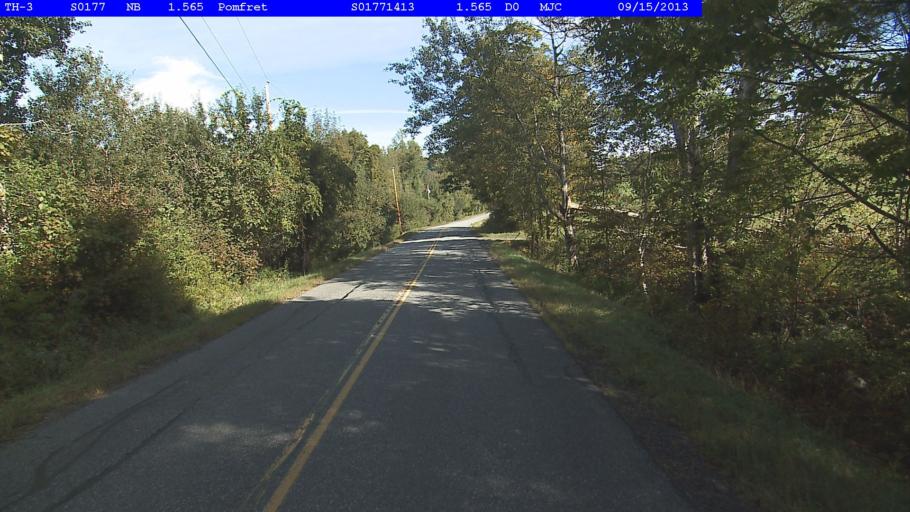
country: US
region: Vermont
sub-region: Windsor County
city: Woodstock
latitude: 43.7433
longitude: -72.4926
